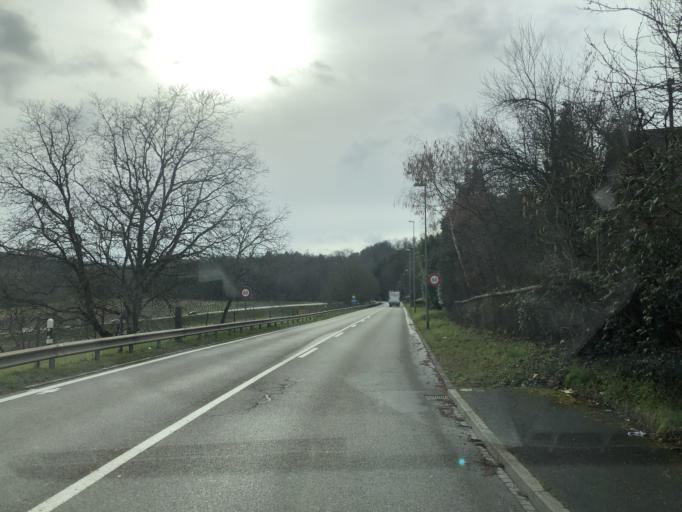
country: CH
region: Aargau
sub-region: Bezirk Brugg
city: Windisch
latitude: 47.4787
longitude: 8.2235
